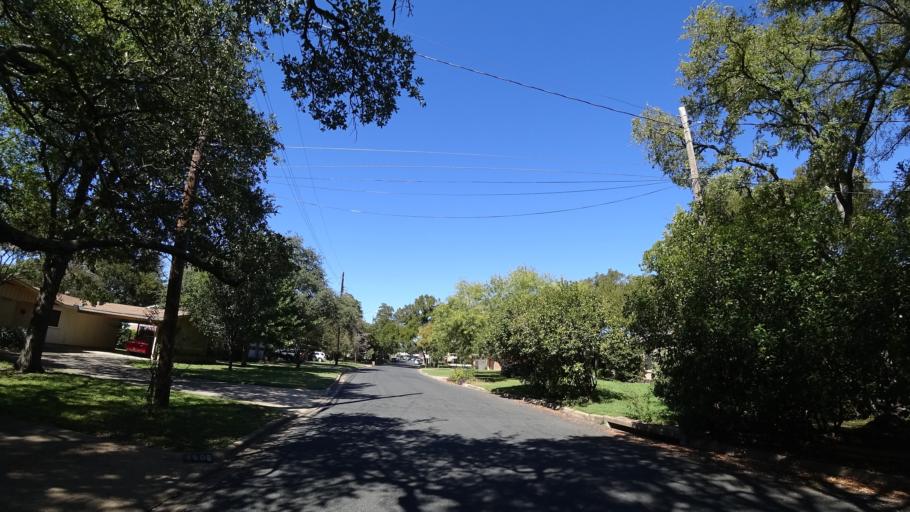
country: US
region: Texas
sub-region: Travis County
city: Rollingwood
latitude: 30.2294
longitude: -97.7949
